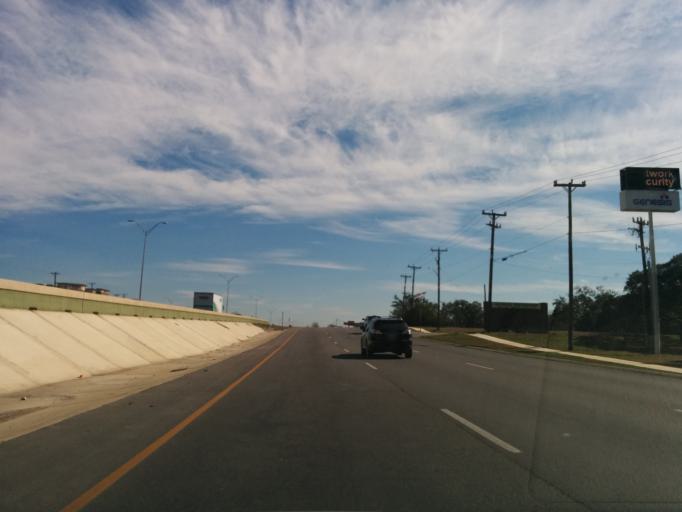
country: US
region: Texas
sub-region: Bexar County
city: Hollywood Park
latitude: 29.6091
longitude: -98.4861
